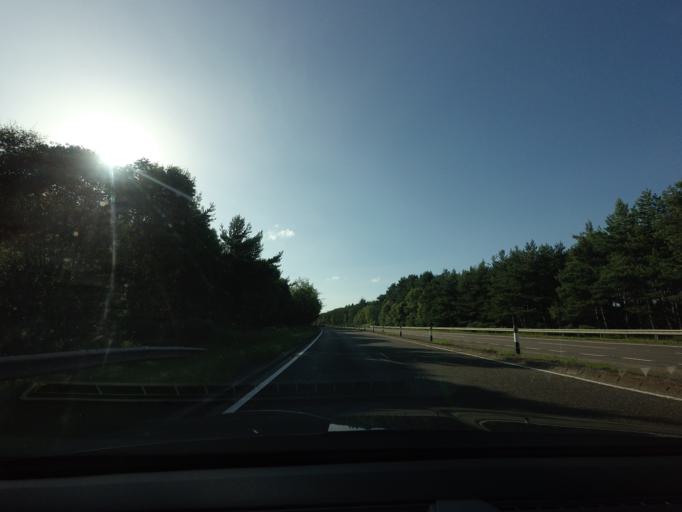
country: GB
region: Scotland
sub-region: Highland
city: Inverness
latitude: 57.5148
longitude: -4.2926
